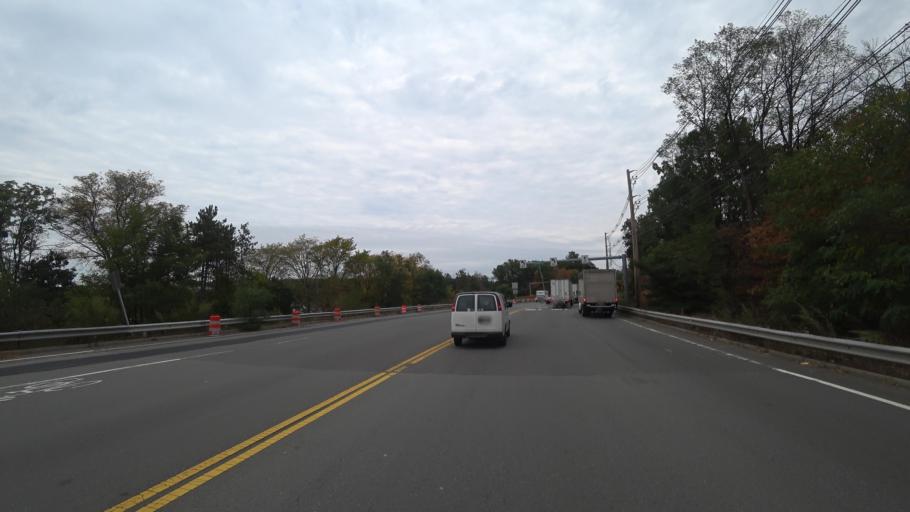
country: US
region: Massachusetts
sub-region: Middlesex County
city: Wilmington
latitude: 42.5863
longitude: -71.1566
